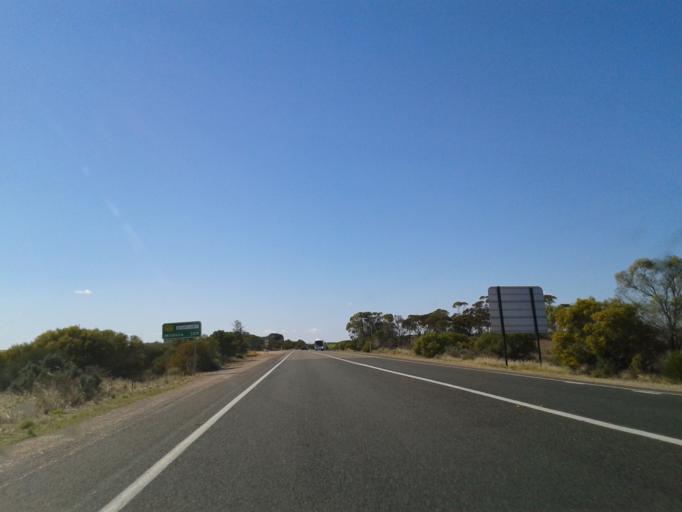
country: AU
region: South Australia
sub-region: Renmark Paringa
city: Renmark
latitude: -34.2459
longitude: 140.8368
